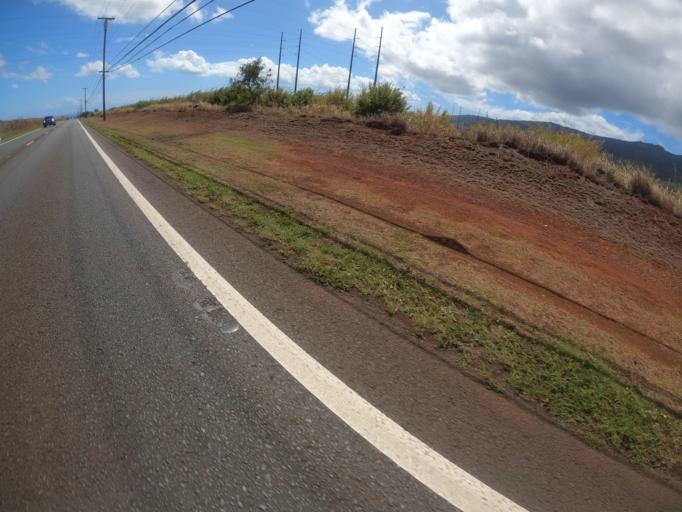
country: US
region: Hawaii
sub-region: Honolulu County
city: Village Park
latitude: 21.4146
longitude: -158.0463
